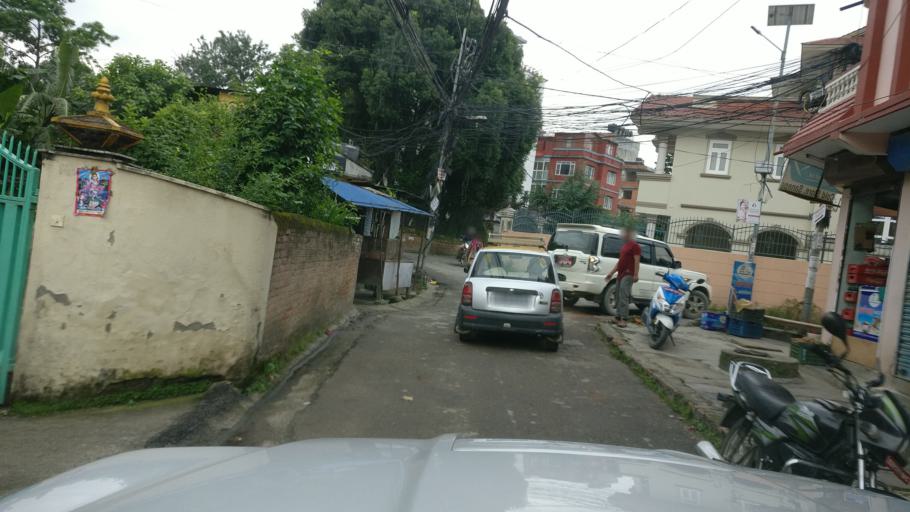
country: NP
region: Central Region
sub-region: Bagmati Zone
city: Patan
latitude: 27.6835
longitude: 85.3098
